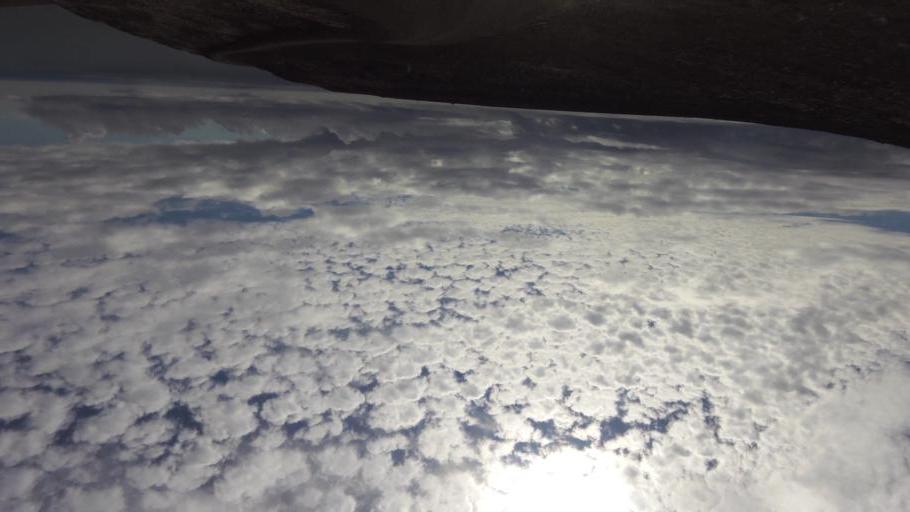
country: IS
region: West
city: Olafsvik
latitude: 65.6232
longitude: -24.2861
